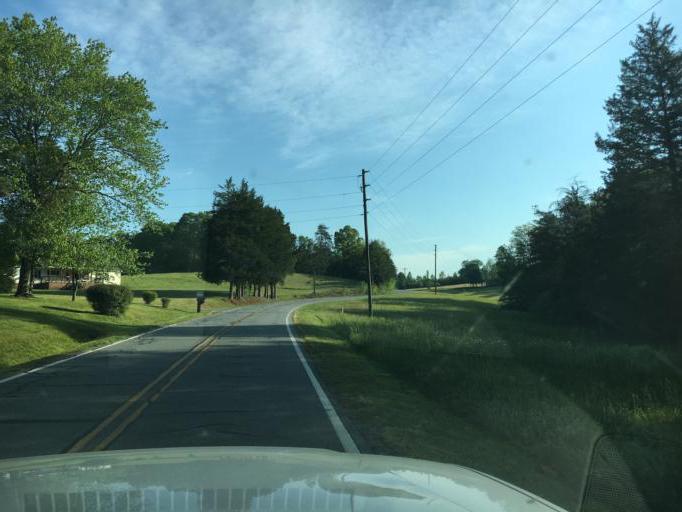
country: US
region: North Carolina
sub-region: Rutherford County
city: Rutherfordton
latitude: 35.3134
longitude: -81.9927
